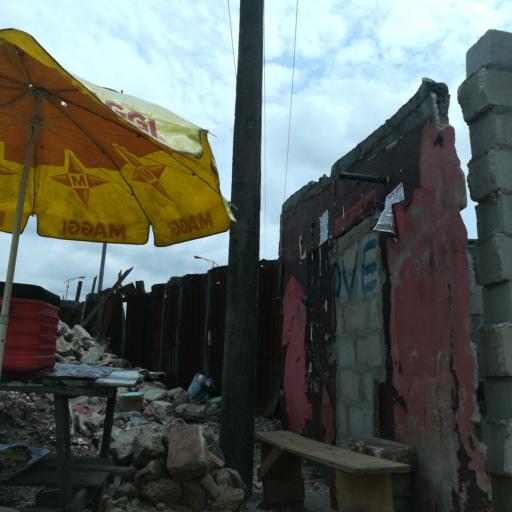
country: NG
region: Rivers
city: Port Harcourt
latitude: 4.7961
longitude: 7.0244
